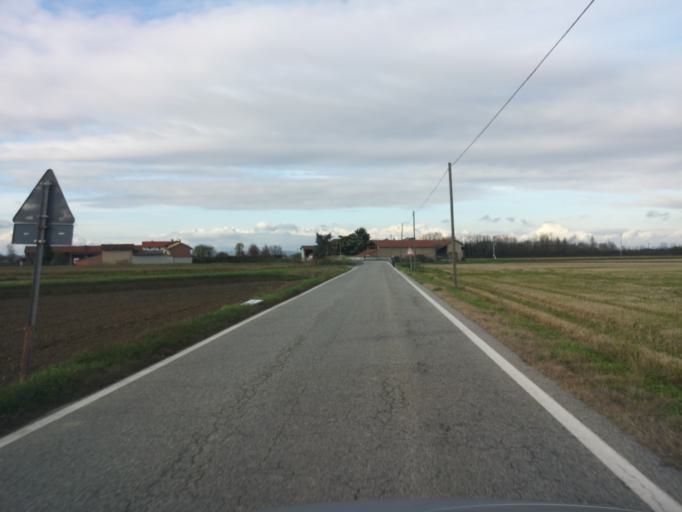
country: IT
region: Piedmont
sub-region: Provincia di Vercelli
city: Crova
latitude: 45.3238
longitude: 8.1933
